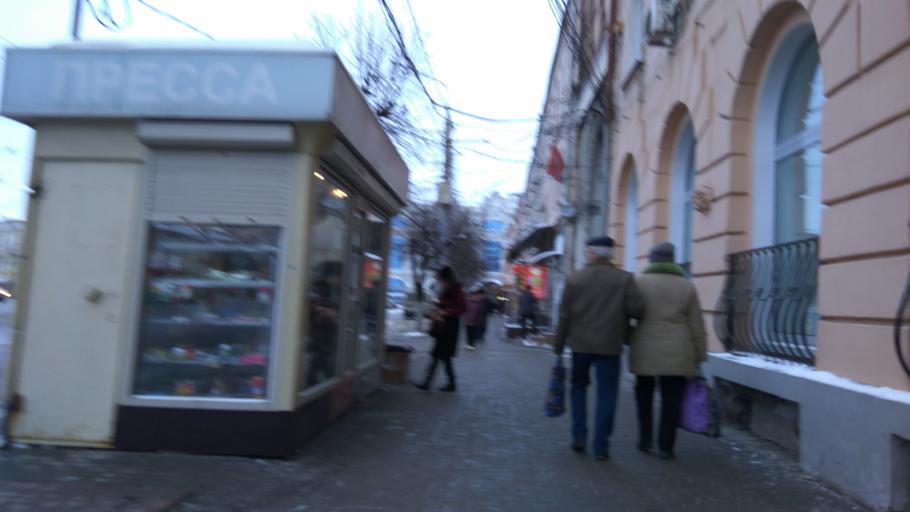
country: RU
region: Tula
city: Tula
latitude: 54.1942
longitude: 37.6119
